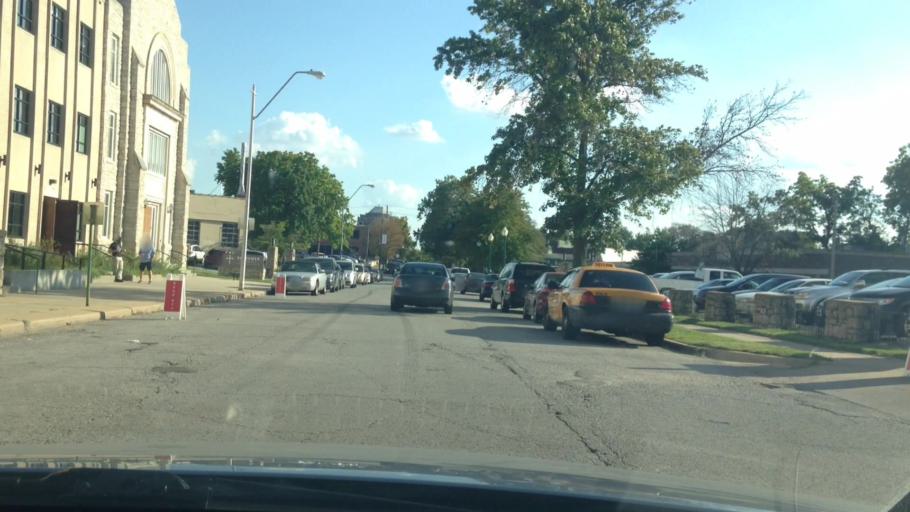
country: US
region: Kansas
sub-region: Johnson County
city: Westwood
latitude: 39.0561
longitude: -94.5873
